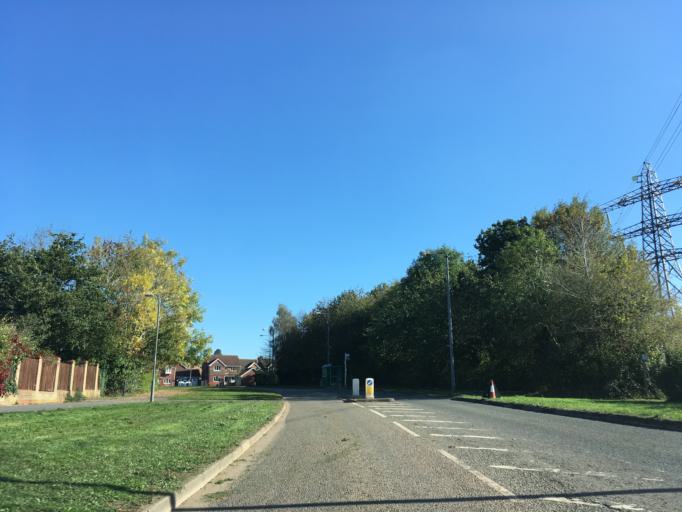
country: GB
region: England
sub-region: South Gloucestershire
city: Yate
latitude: 51.5536
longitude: -2.4133
